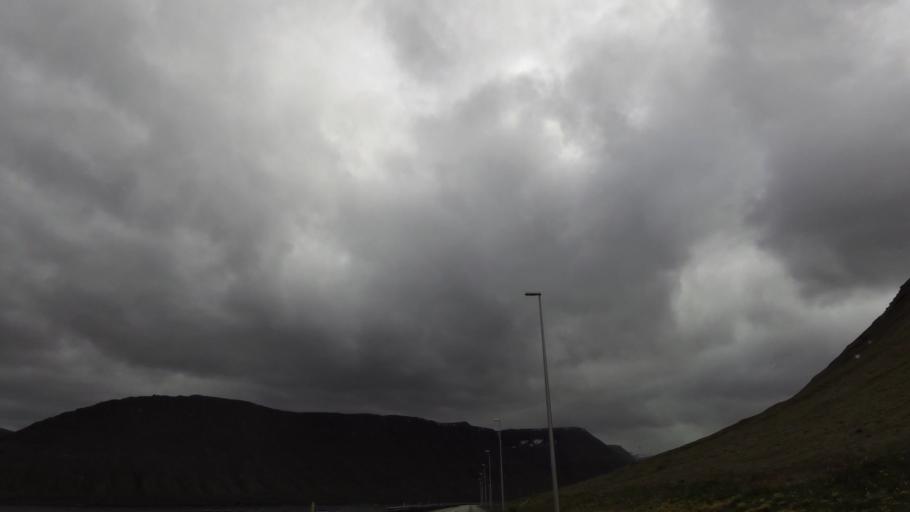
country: IS
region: Westfjords
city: Isafjoerdur
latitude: 66.1026
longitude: -23.1097
